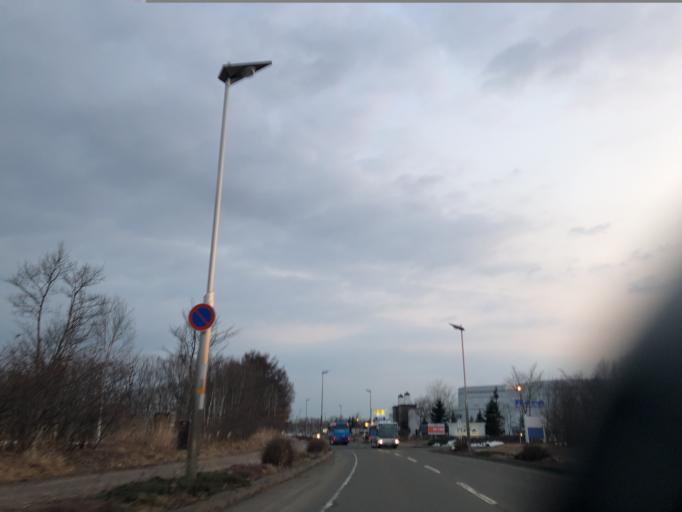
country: JP
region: Hokkaido
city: Chitose
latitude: 42.8137
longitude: 141.6782
